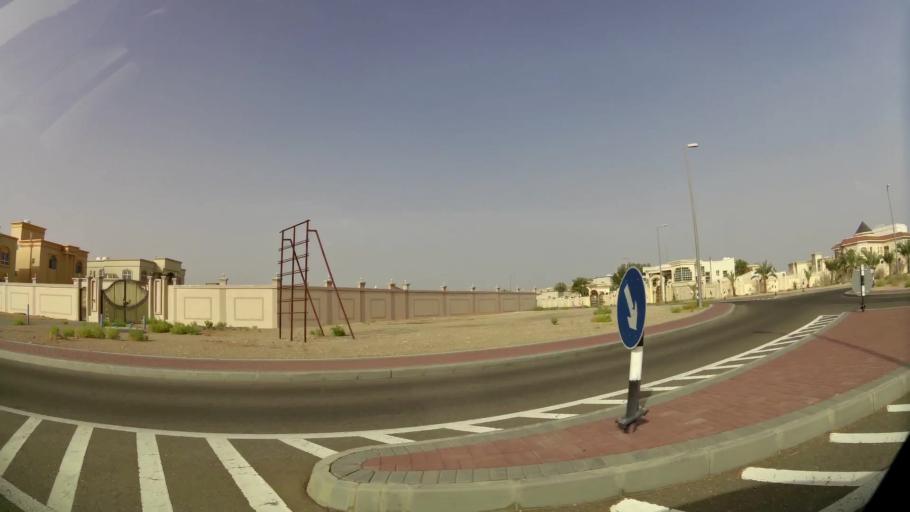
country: AE
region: Abu Dhabi
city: Al Ain
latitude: 24.2069
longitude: 55.6247
